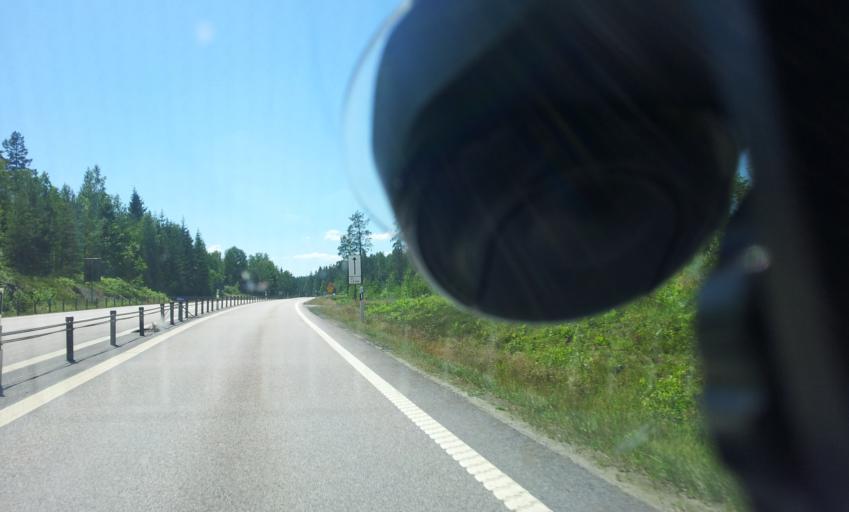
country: SE
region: Kalmar
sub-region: Vasterviks Kommun
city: Forserum
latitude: 58.0416
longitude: 16.5222
